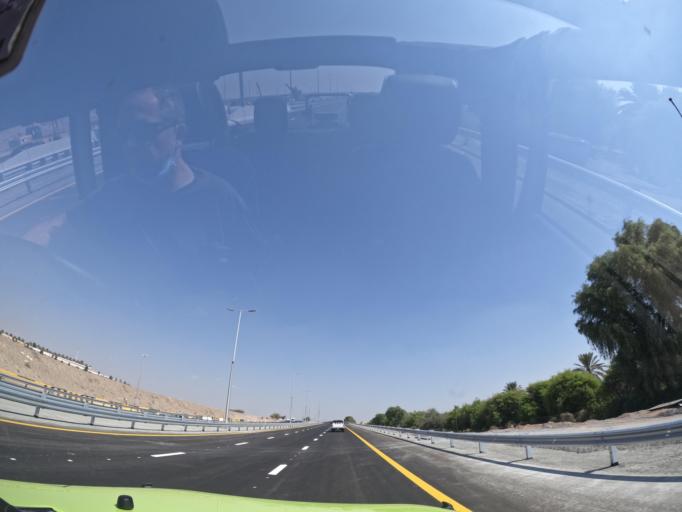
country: AE
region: Ash Shariqah
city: Adh Dhayd
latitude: 24.7771
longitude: 55.8137
